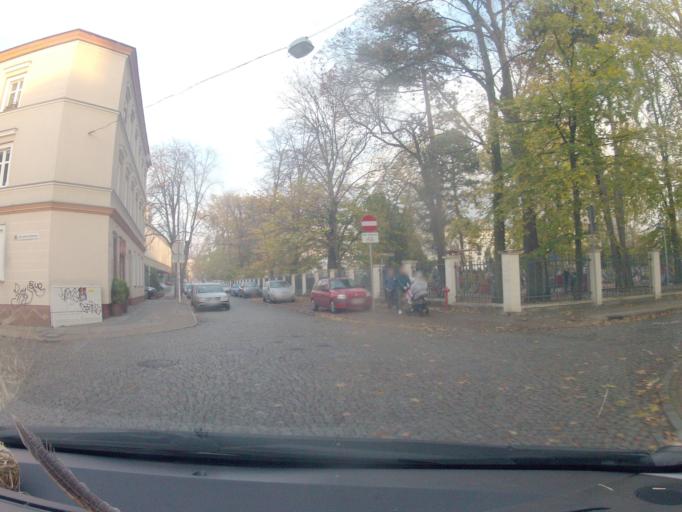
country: PL
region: Opole Voivodeship
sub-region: Powiat opolski
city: Opole
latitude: 50.6652
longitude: 17.9203
